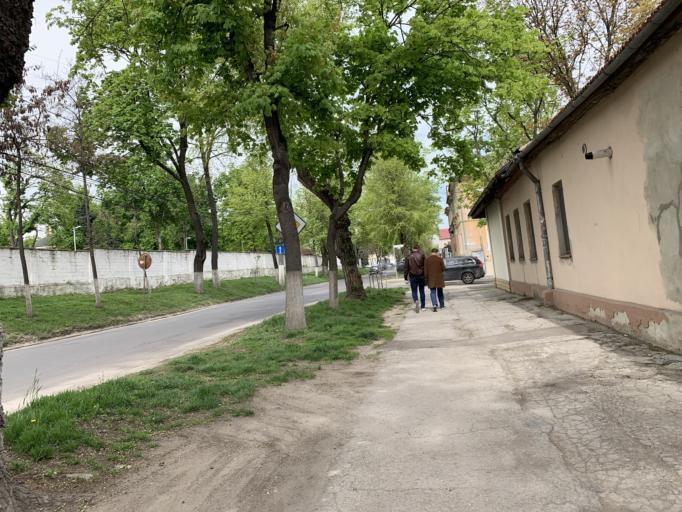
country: MD
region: Chisinau
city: Chisinau
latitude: 47.0116
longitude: 28.8323
